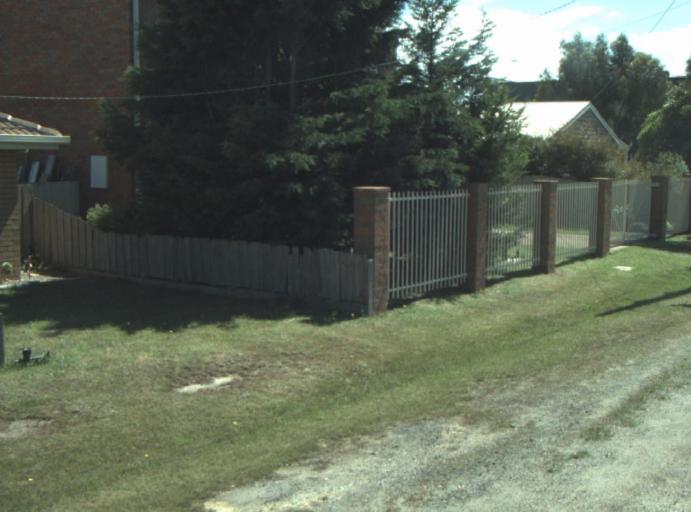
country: AU
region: Victoria
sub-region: Queenscliffe
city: Queenscliff
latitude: -38.1743
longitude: 144.7096
